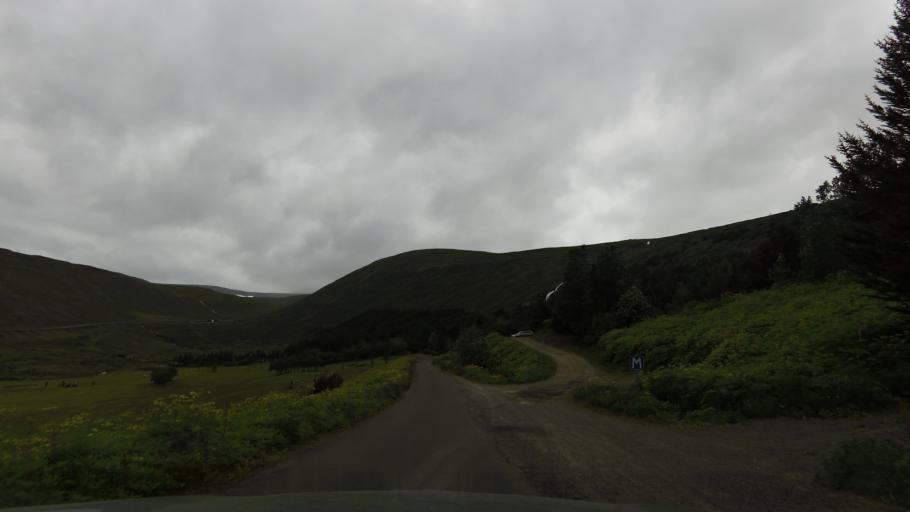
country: IS
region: Westfjords
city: Isafjoerdur
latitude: 66.0607
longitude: -23.1949
